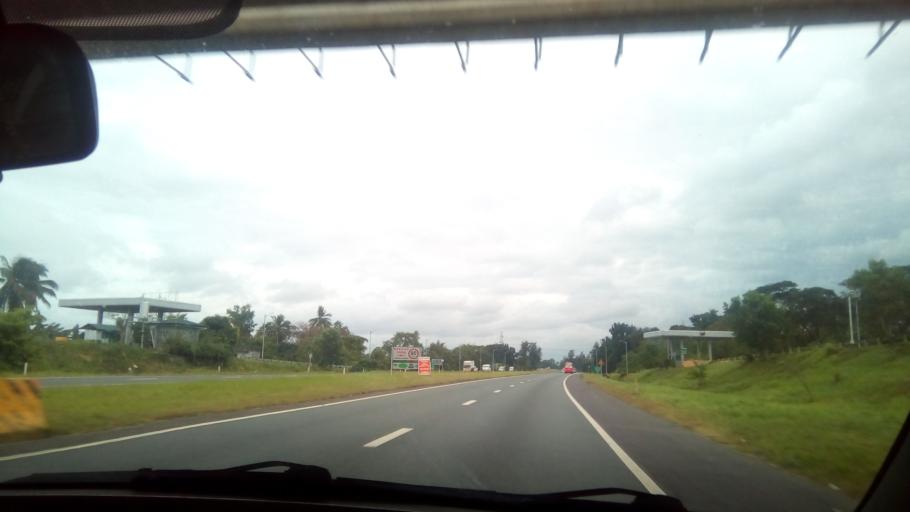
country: PH
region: Calabarzon
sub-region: Province of Batangas
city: Tanauan
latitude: 14.0861
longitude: 121.1328
